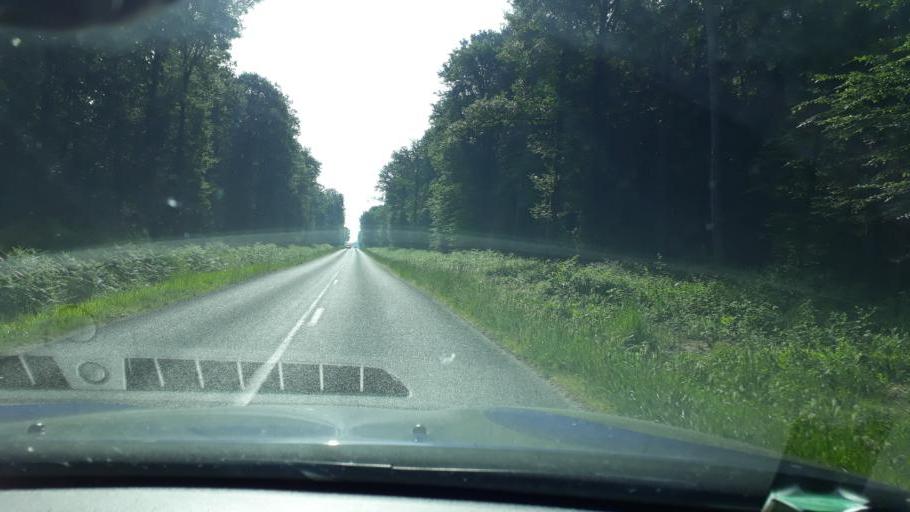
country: FR
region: Centre
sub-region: Departement du Loiret
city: Chilleurs-aux-Bois
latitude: 48.0618
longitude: 2.2312
